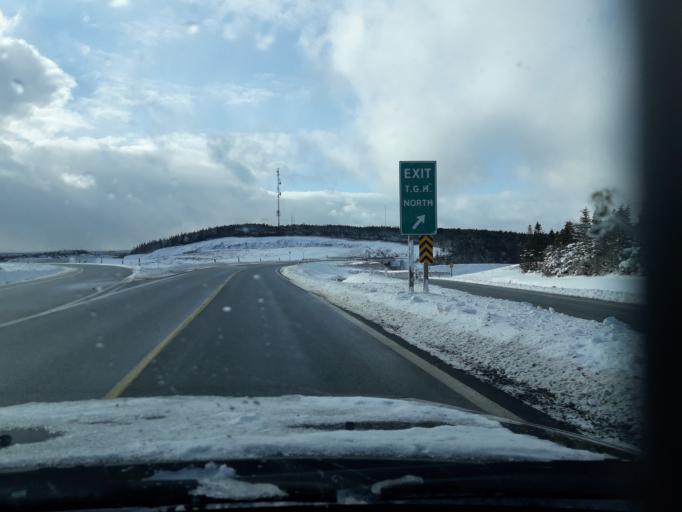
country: CA
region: Newfoundland and Labrador
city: Mount Pearl
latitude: 47.5506
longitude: -52.7613
